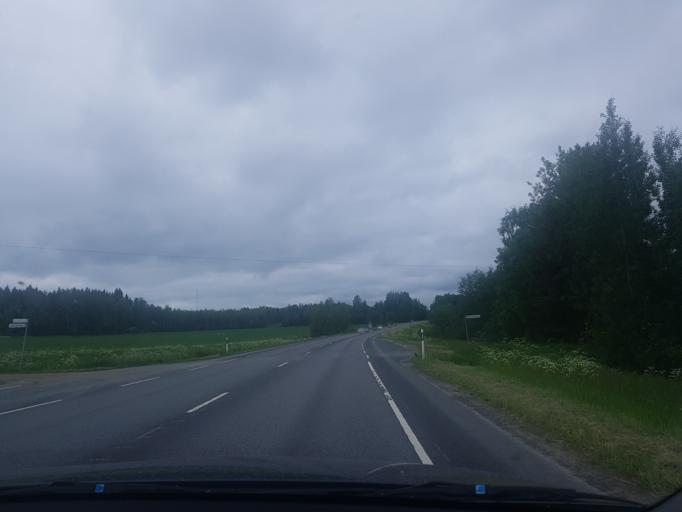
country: FI
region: Pirkanmaa
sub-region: Tampere
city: Paelkaene
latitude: 61.3919
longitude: 24.2167
